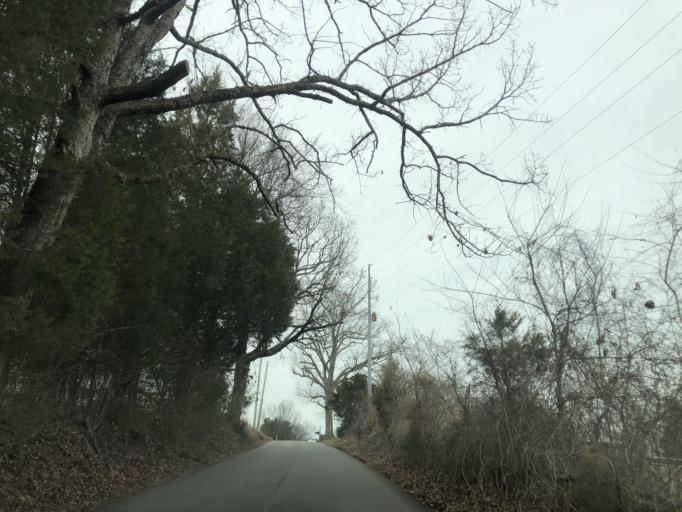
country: US
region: Tennessee
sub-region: Robertson County
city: Greenbrier
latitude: 36.4491
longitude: -86.7942
